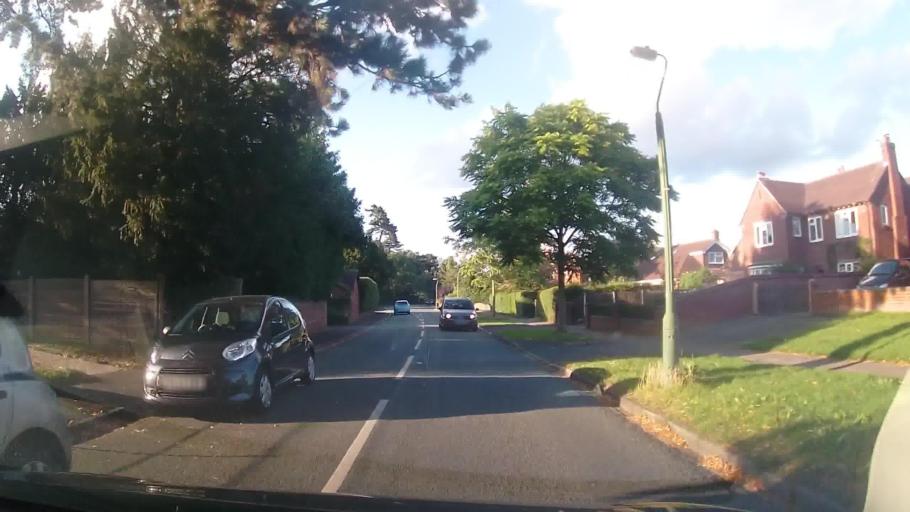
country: GB
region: England
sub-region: Shropshire
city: Shrewsbury
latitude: 52.6965
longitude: -2.7310
